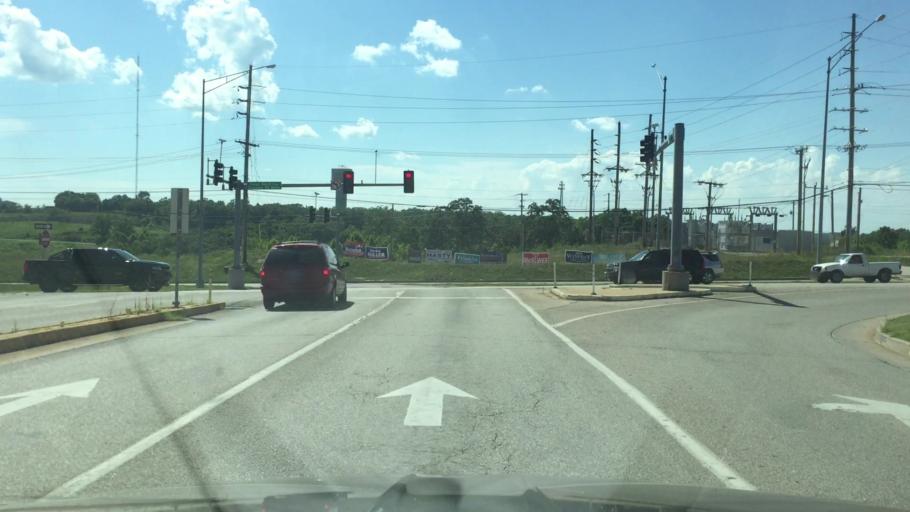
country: US
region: Missouri
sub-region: Miller County
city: Lake Ozark
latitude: 38.1567
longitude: -92.6047
